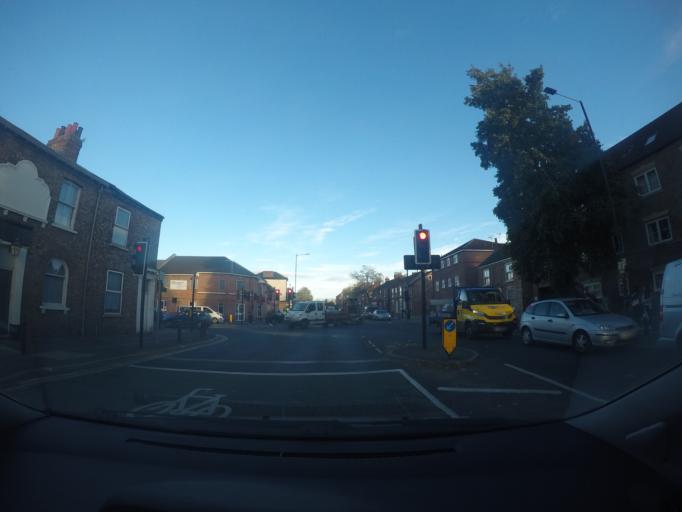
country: GB
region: England
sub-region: City of York
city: York
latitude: 53.9547
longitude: -1.0681
